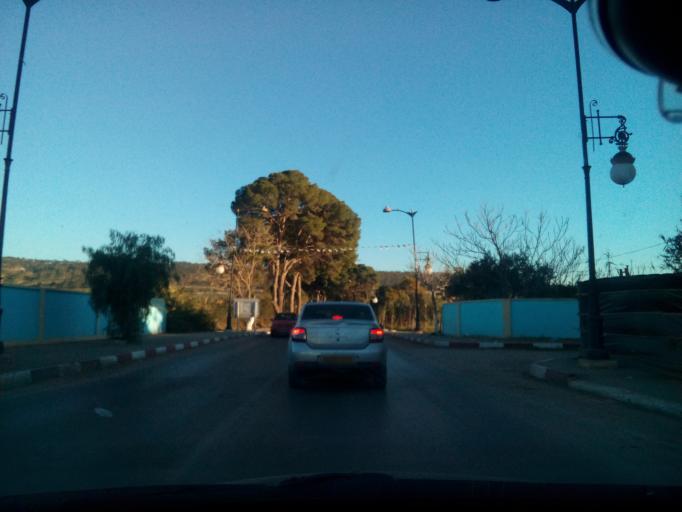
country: DZ
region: Mostaganem
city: Mostaganem
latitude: 35.7771
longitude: 0.1943
